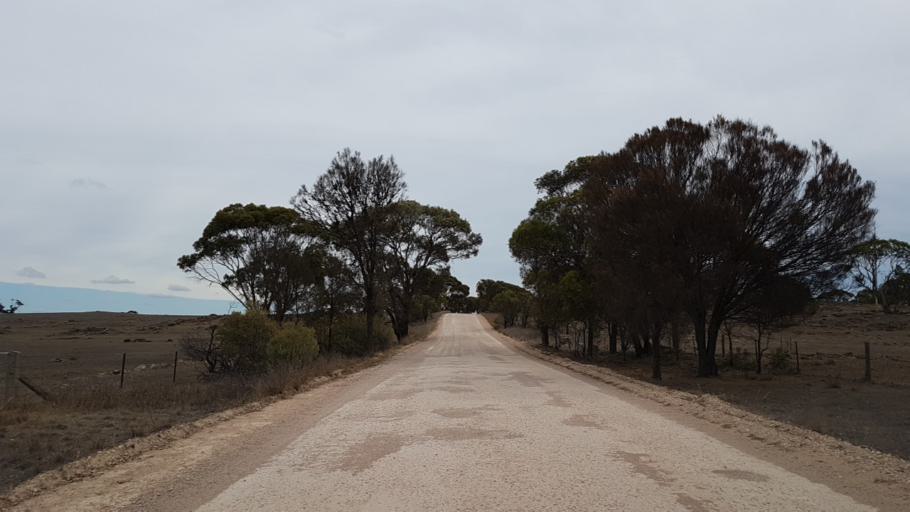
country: AU
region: South Australia
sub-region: Mount Barker
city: Callington
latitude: -35.0060
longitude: 139.0764
